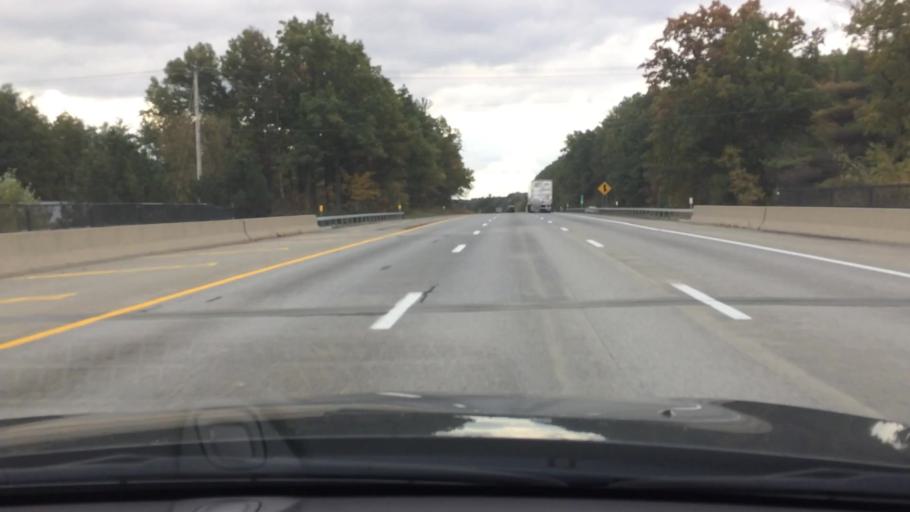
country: US
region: New York
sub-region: Saratoga County
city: Country Knolls
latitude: 42.9371
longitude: -73.8047
